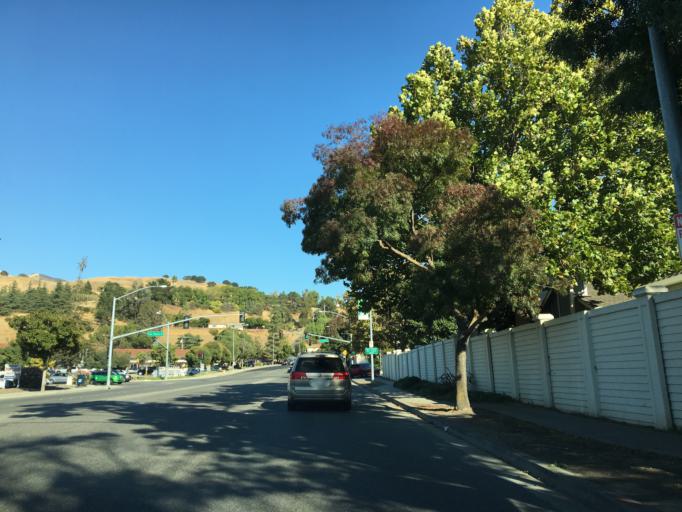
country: US
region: California
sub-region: Santa Clara County
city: Milpitas
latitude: 37.4474
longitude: -121.8886
